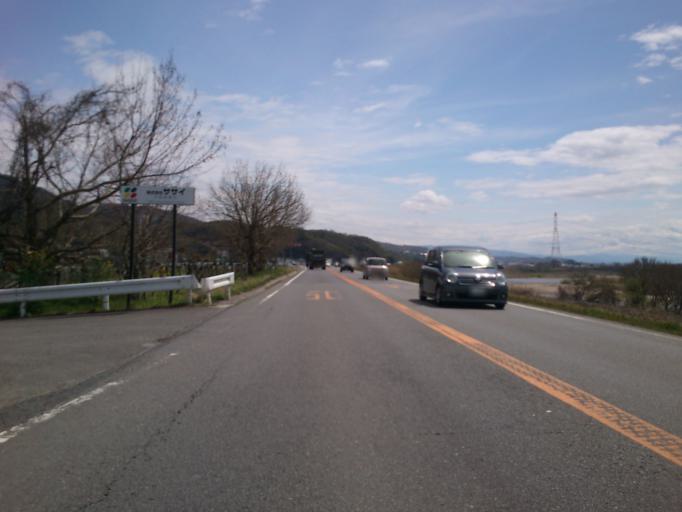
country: JP
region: Kyoto
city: Tanabe
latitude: 34.8155
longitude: 135.8012
